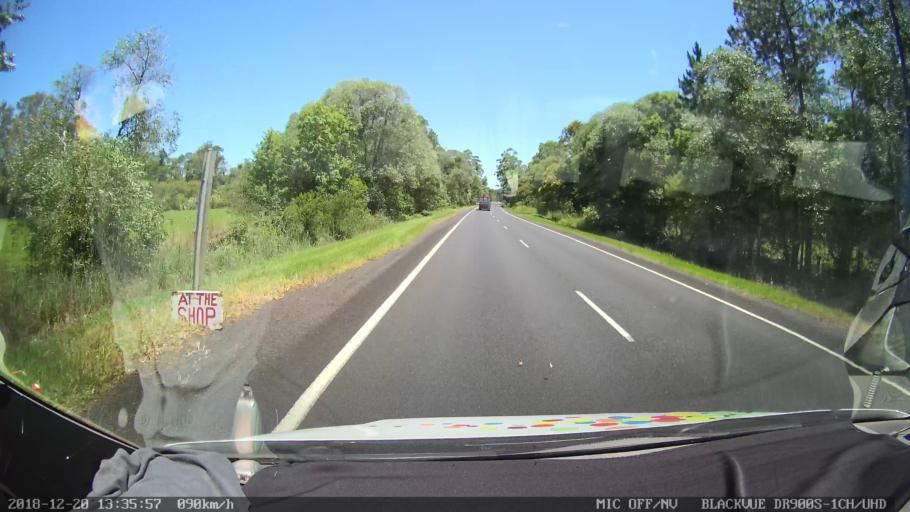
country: AU
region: New South Wales
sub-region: Clarence Valley
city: Maclean
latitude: -29.2763
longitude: 152.9913
